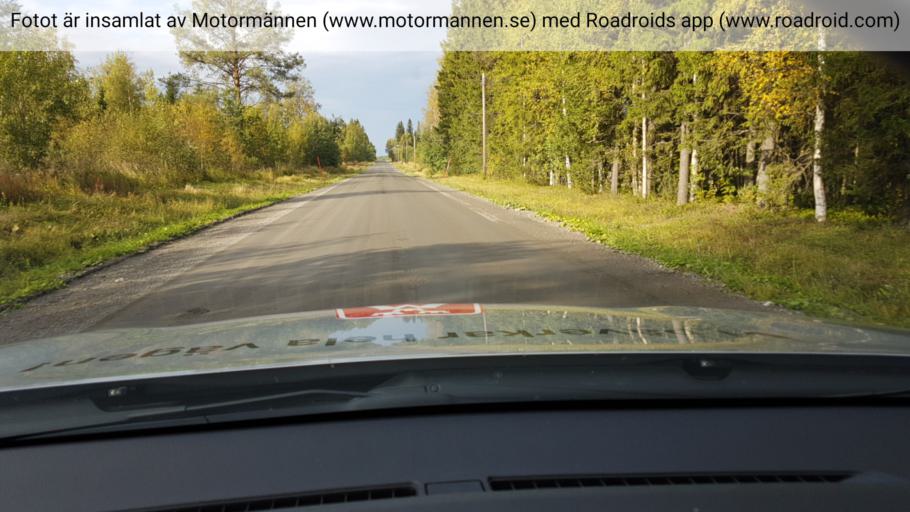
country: SE
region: Jaemtland
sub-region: Stroemsunds Kommun
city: Stroemsund
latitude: 64.0229
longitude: 15.8114
